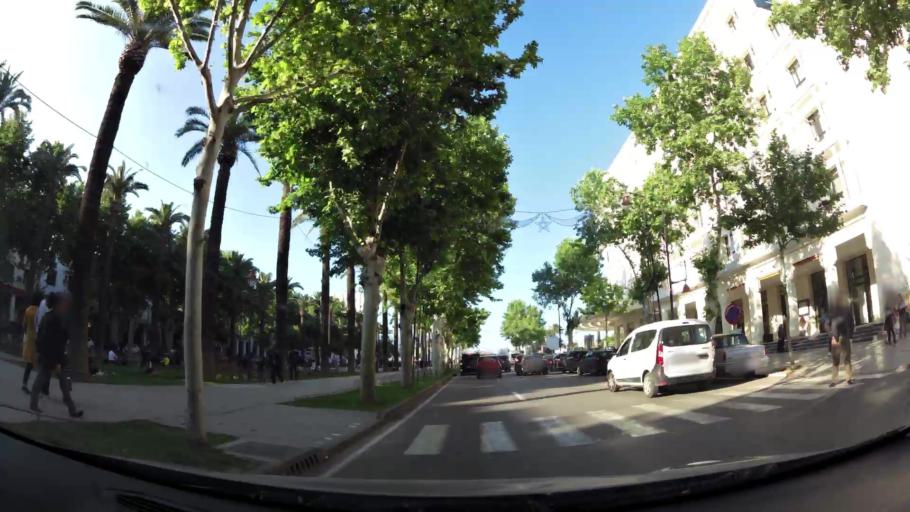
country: MA
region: Fes-Boulemane
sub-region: Fes
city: Fes
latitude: 34.0434
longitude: -4.9978
